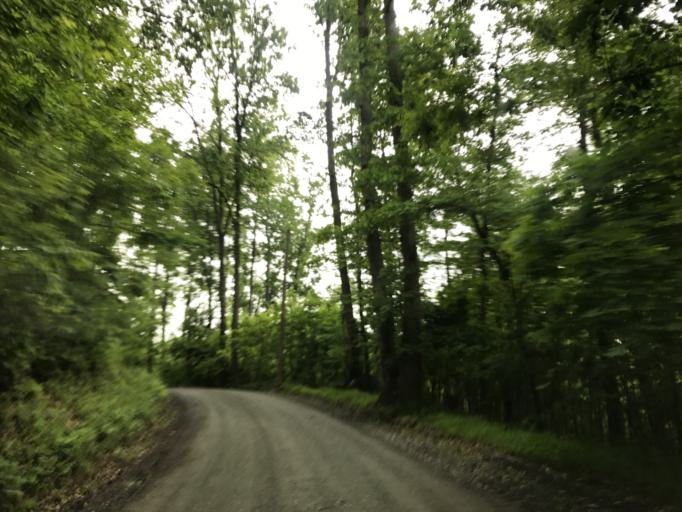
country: US
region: Maryland
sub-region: Harford County
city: Jarrettsville
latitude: 39.6844
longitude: -76.5089
